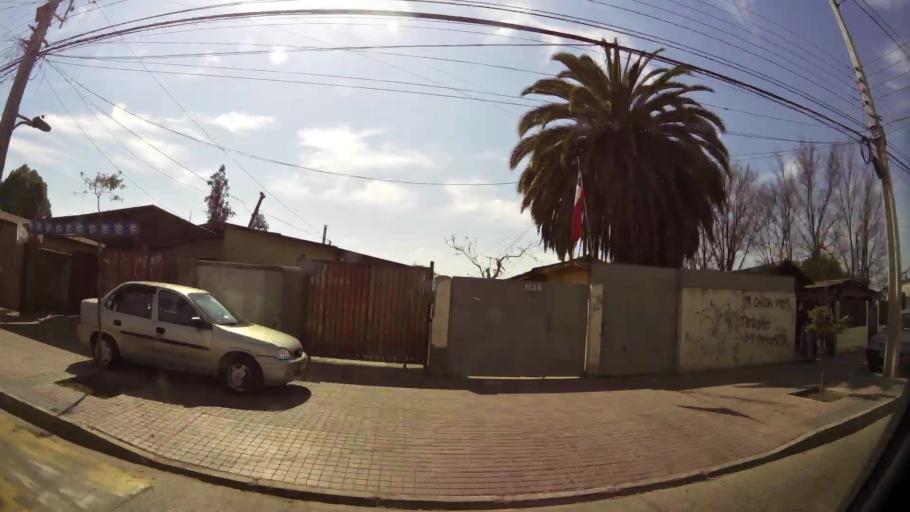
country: CL
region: Santiago Metropolitan
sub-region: Provincia de Talagante
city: Talagante
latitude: -33.6691
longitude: -70.9305
